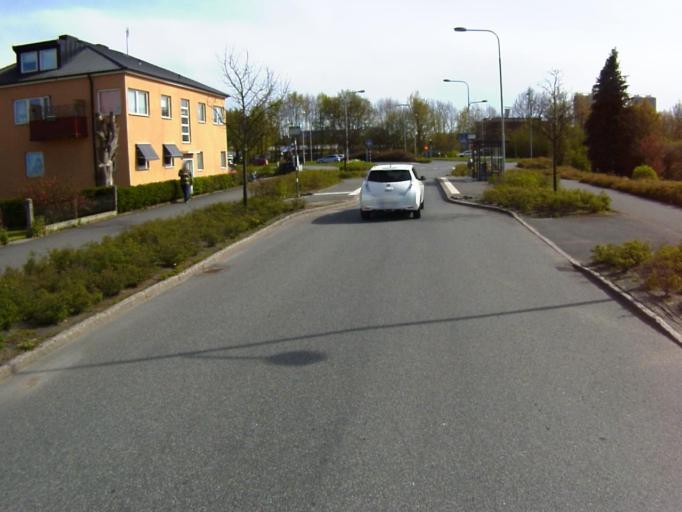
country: SE
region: Skane
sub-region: Kristianstads Kommun
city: Kristianstad
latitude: 56.0449
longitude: 14.1545
